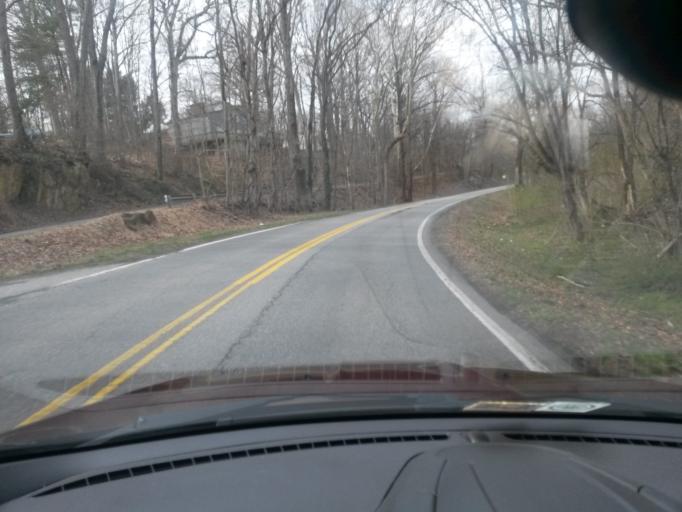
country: US
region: Virginia
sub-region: Roanoke County
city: Cave Spring
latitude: 37.2463
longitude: -80.0044
